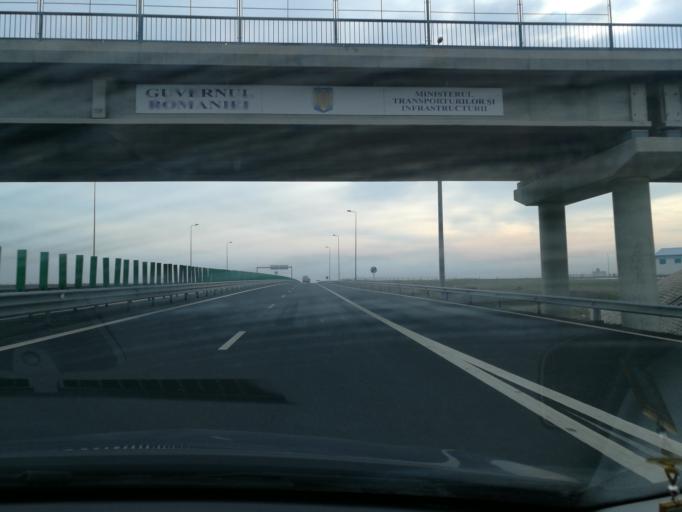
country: RO
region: Constanta
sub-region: Municipiul Medgidia
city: Valea Dacilor
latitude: 44.1747
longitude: 28.3226
